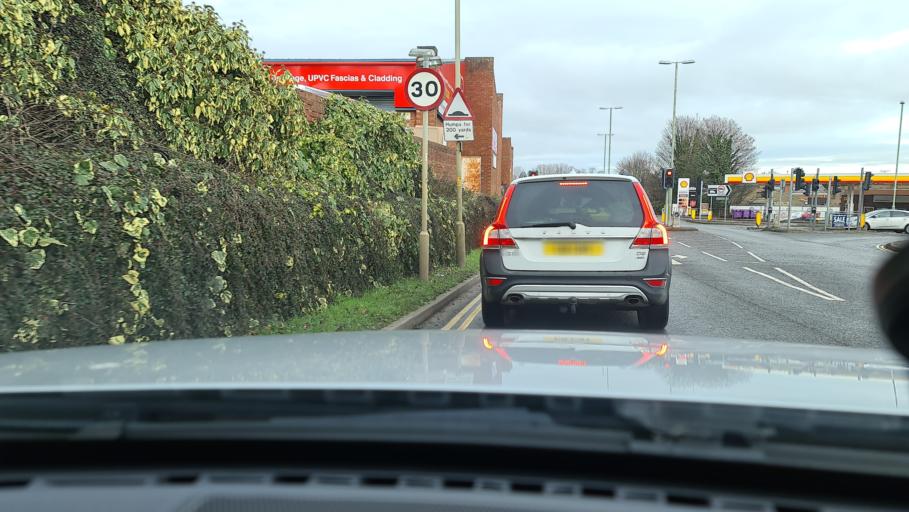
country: GB
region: England
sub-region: Oxfordshire
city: Banbury
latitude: 52.0576
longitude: -1.3332
